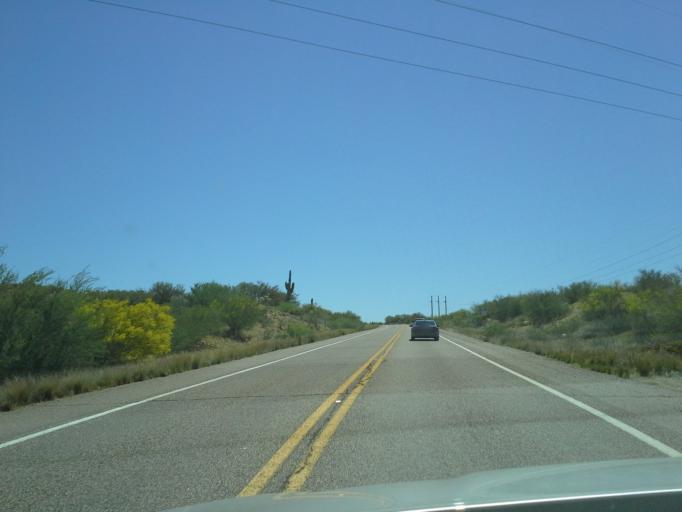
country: US
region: Arizona
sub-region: Pinal County
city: Kearny
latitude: 33.1202
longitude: -110.9740
